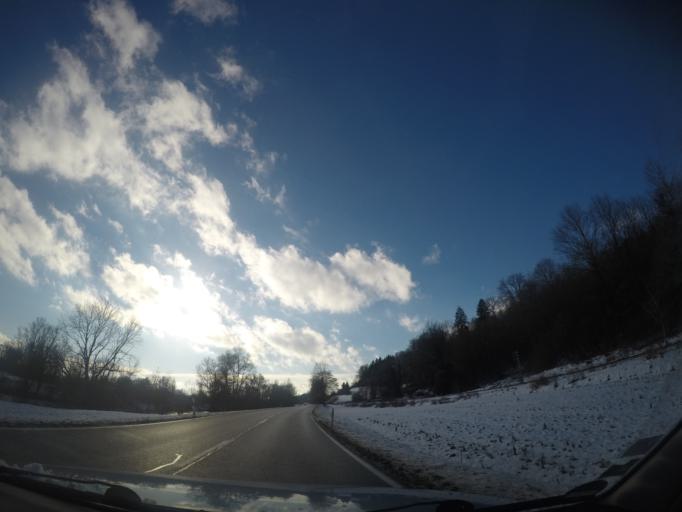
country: DE
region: Baden-Wuerttemberg
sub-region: Tuebingen Region
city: Rottenacker
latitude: 48.2422
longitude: 9.7068
